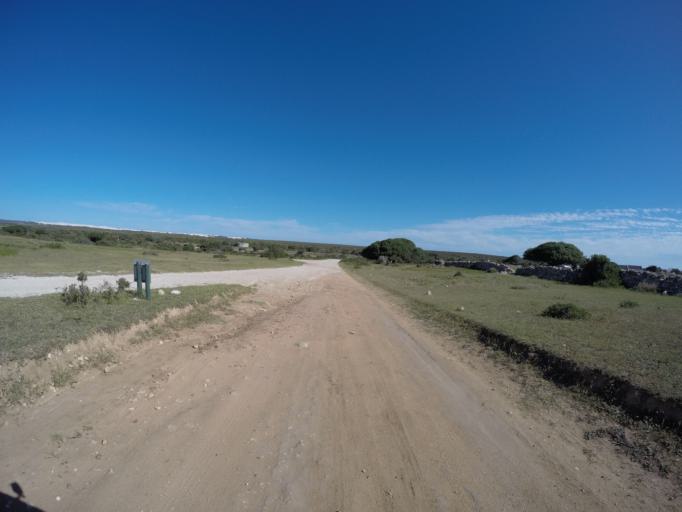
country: ZA
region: Western Cape
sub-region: Overberg District Municipality
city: Bredasdorp
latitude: -34.4544
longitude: 20.4094
